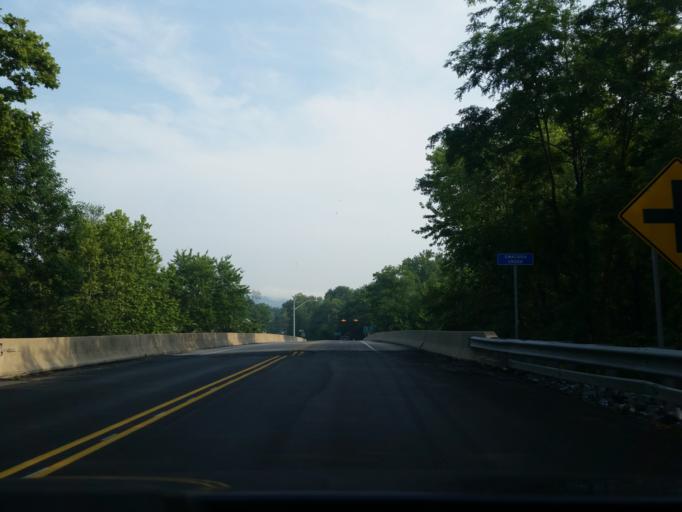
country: US
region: Pennsylvania
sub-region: Lebanon County
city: Palmyra
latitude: 40.4026
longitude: -76.5766
